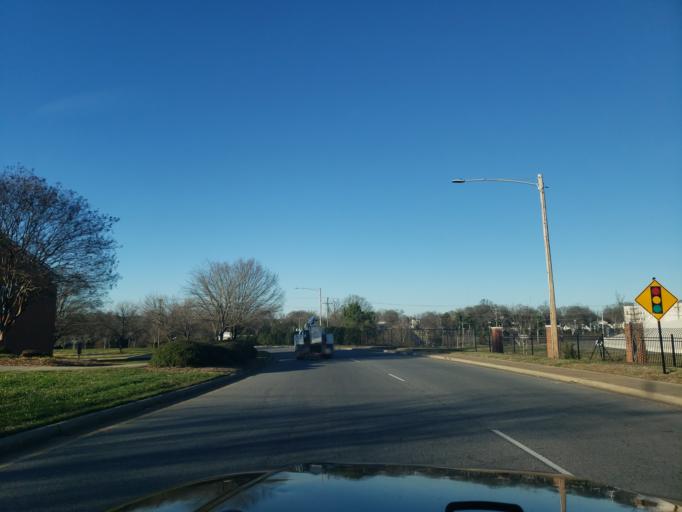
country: US
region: North Carolina
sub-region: Gaston County
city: Gastonia
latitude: 35.2653
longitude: -81.1857
